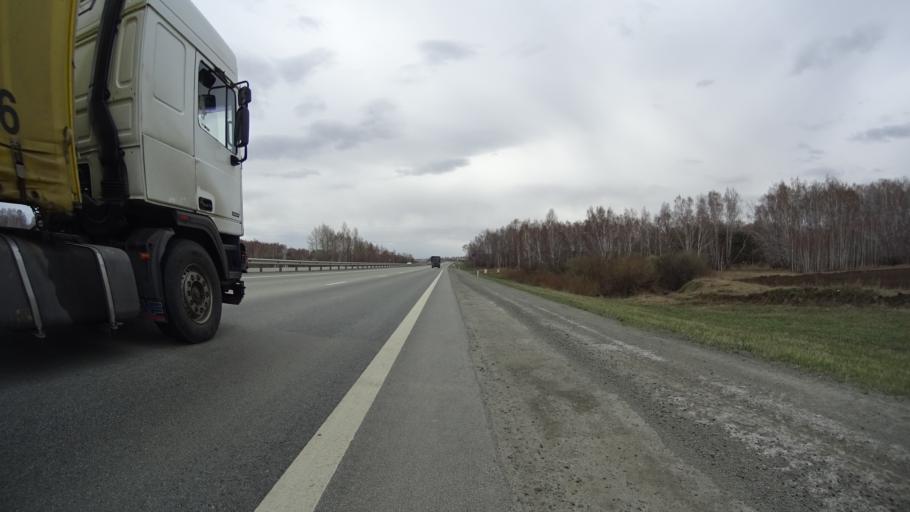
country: RU
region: Chelyabinsk
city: Yemanzhelinka
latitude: 54.8288
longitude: 61.3110
